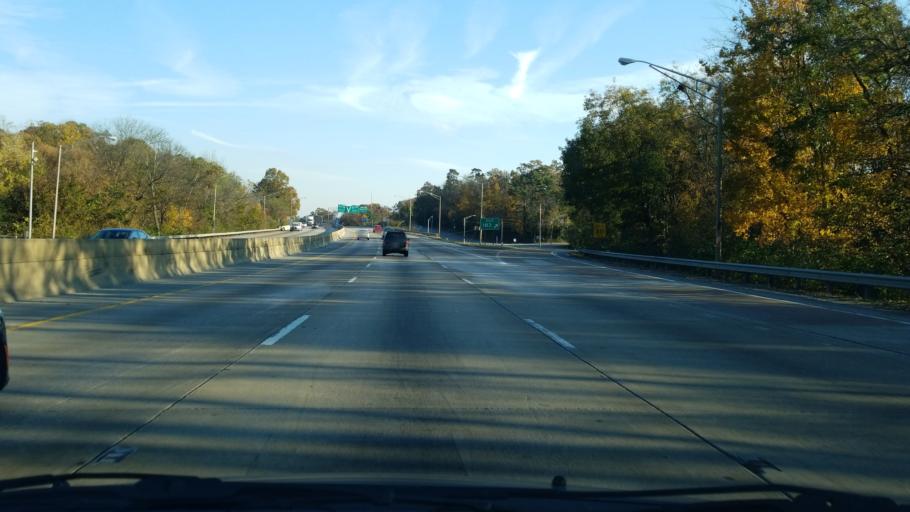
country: US
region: Tennessee
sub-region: Hamilton County
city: East Ridge
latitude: 35.0154
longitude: -85.2536
